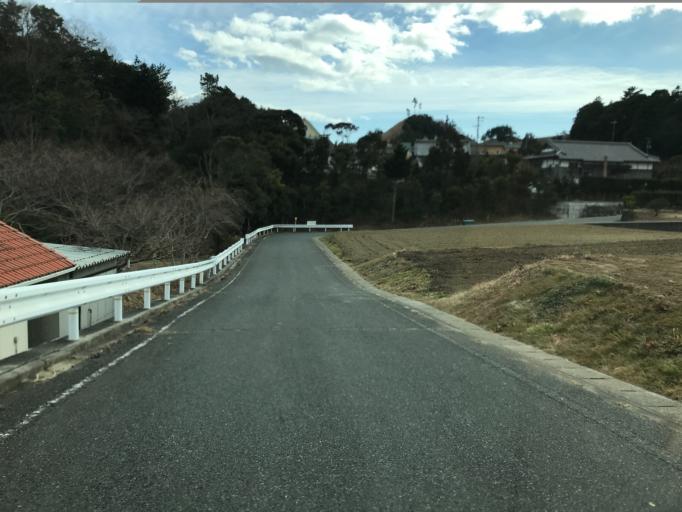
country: JP
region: Fukushima
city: Iwaki
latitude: 37.1693
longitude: 140.9991
